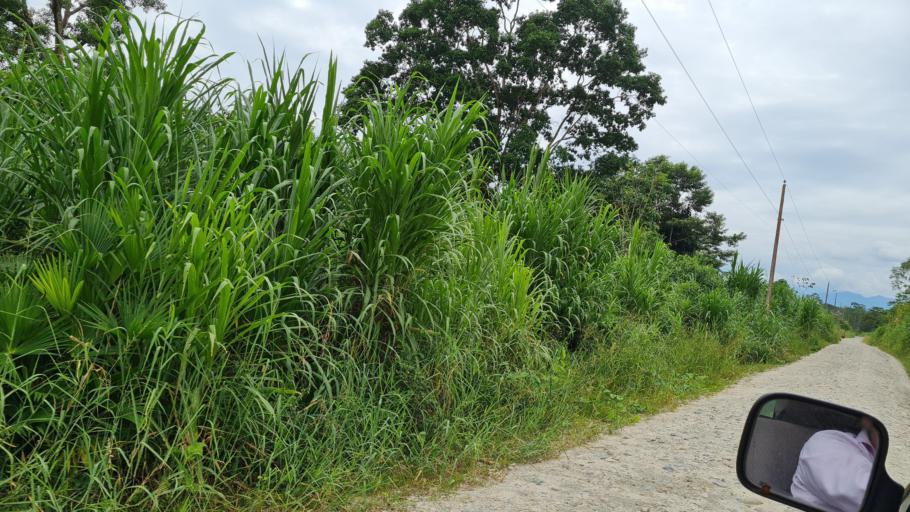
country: EC
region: Napo
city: Tena
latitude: -1.0034
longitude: -77.7699
